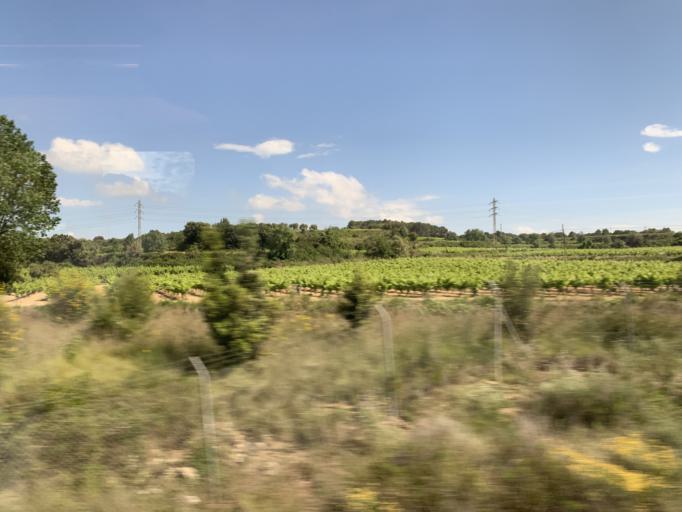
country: ES
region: Catalonia
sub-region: Provincia de Barcelona
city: Vilafranca del Penedes
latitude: 41.3209
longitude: 1.6734
